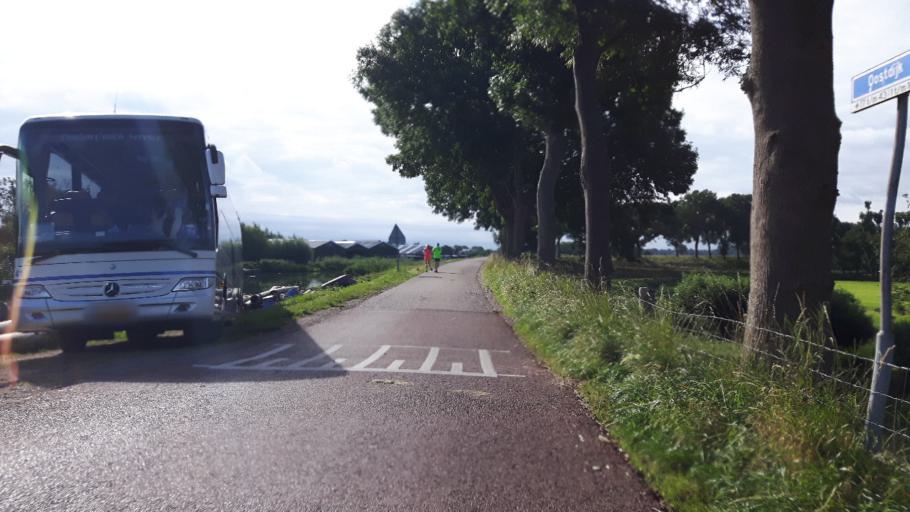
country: NL
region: North Holland
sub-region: Gemeente Purmerend
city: Purmerend
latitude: 52.5483
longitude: 4.9754
